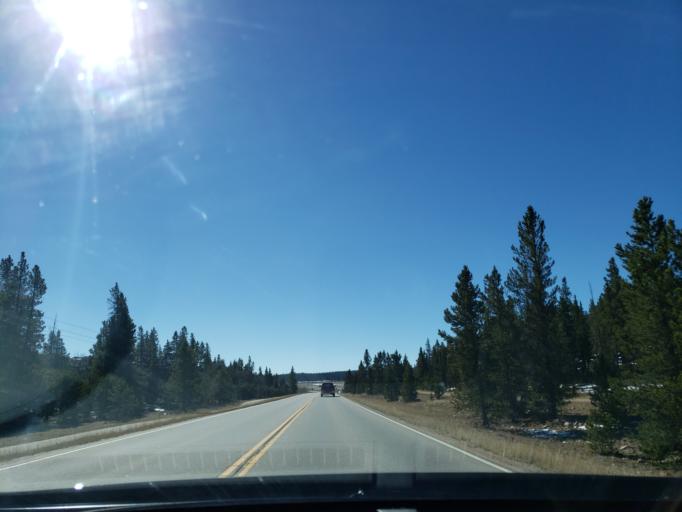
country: US
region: Colorado
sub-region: Park County
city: Fairplay
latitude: 39.2527
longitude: -106.0388
